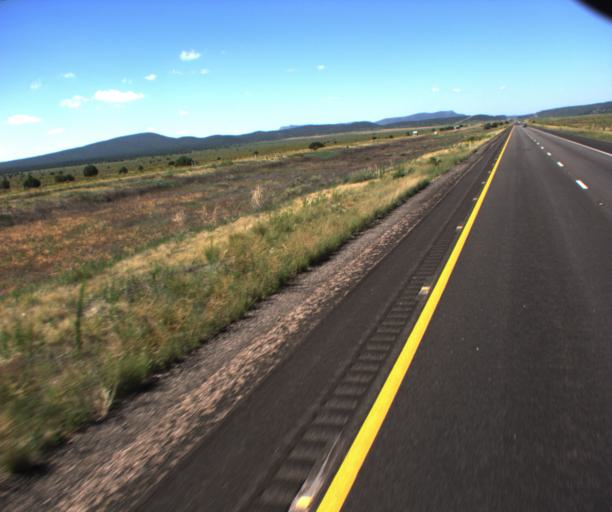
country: US
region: Arizona
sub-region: Mohave County
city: Peach Springs
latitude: 35.2730
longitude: -113.1408
